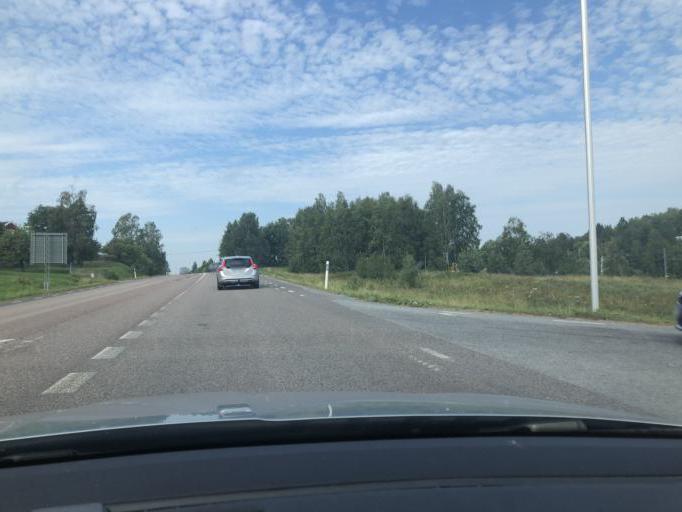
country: SE
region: Vaesternorrland
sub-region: Kramfors Kommun
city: Kramfors
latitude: 62.9039
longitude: 17.8297
